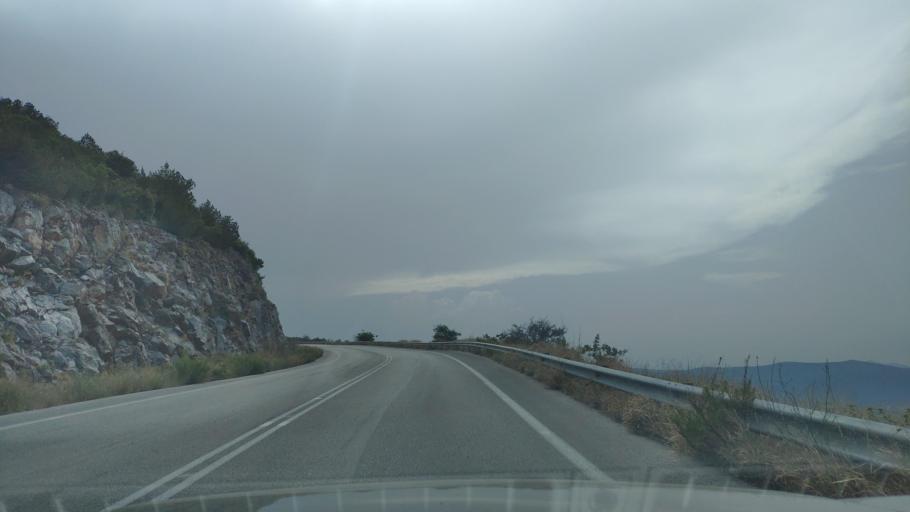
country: GR
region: Peloponnese
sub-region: Nomos Argolidos
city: Didyma
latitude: 37.5084
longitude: 23.1937
